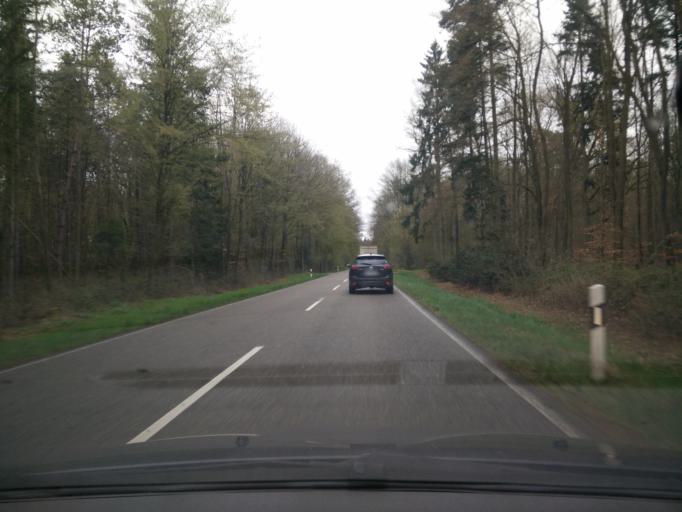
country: DE
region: Rheinland-Pfalz
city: Kandel
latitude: 49.0528
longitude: 8.1938
